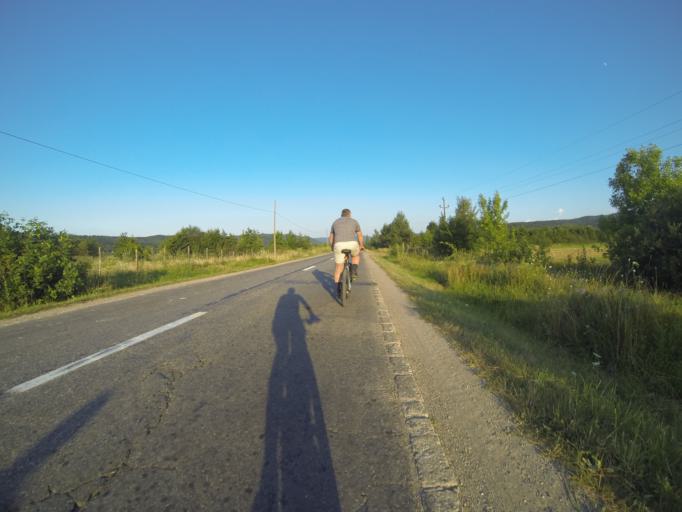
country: RO
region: Brasov
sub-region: Comuna Sinca Veche
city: Sinca Veche
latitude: 45.7481
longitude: 25.1886
